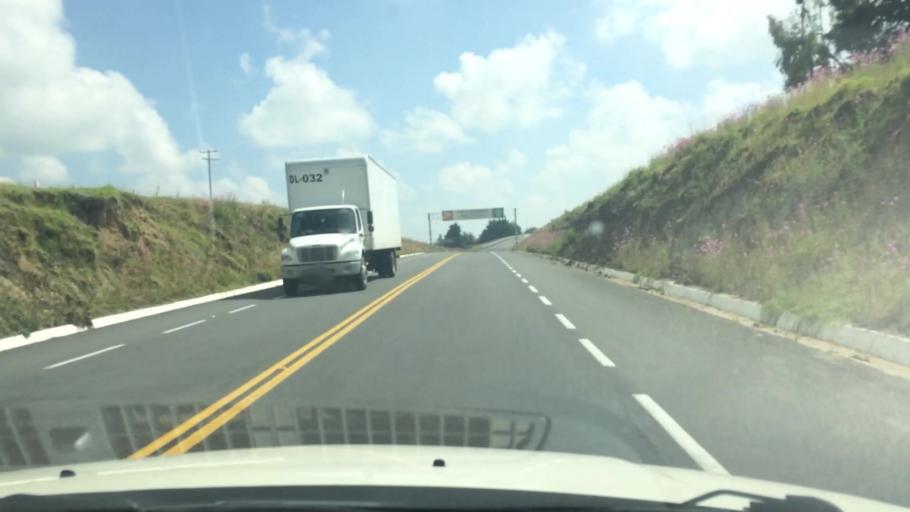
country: MX
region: Mexico
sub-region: Villa Victoria
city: Colonia Doctor Gustavo Baz
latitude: 19.3716
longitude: -99.9320
